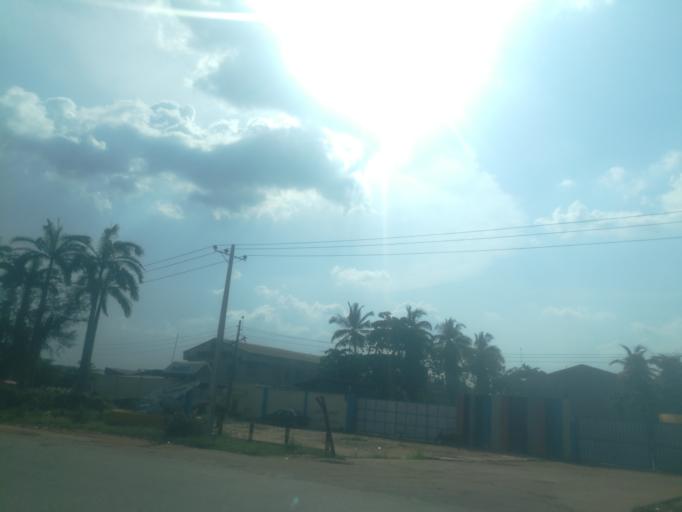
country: NG
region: Ogun
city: Abeokuta
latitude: 7.1124
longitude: 3.2974
